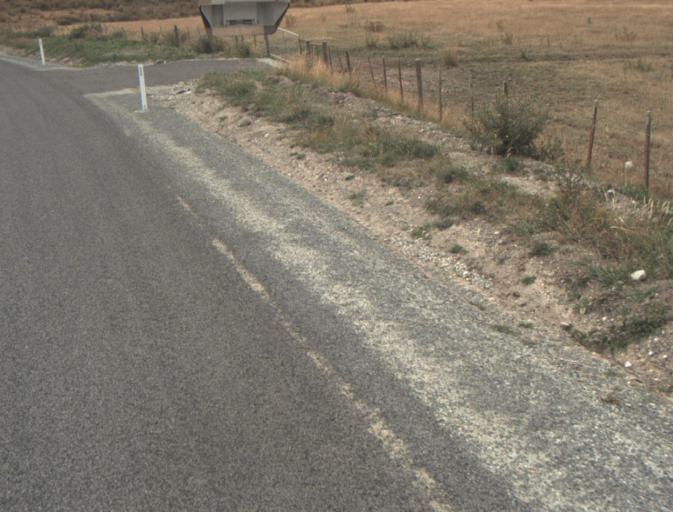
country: AU
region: Tasmania
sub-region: Launceston
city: Mayfield
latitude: -41.1933
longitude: 147.1720
